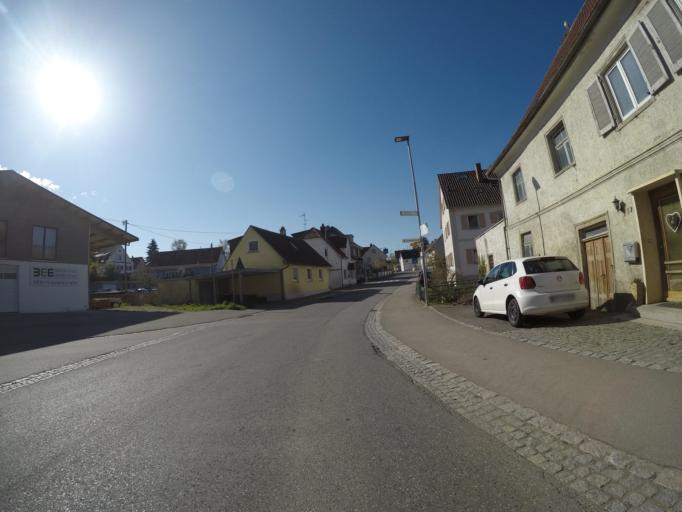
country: DE
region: Baden-Wuerttemberg
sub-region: Tuebingen Region
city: Ebenweiler
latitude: 47.9015
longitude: 9.5130
